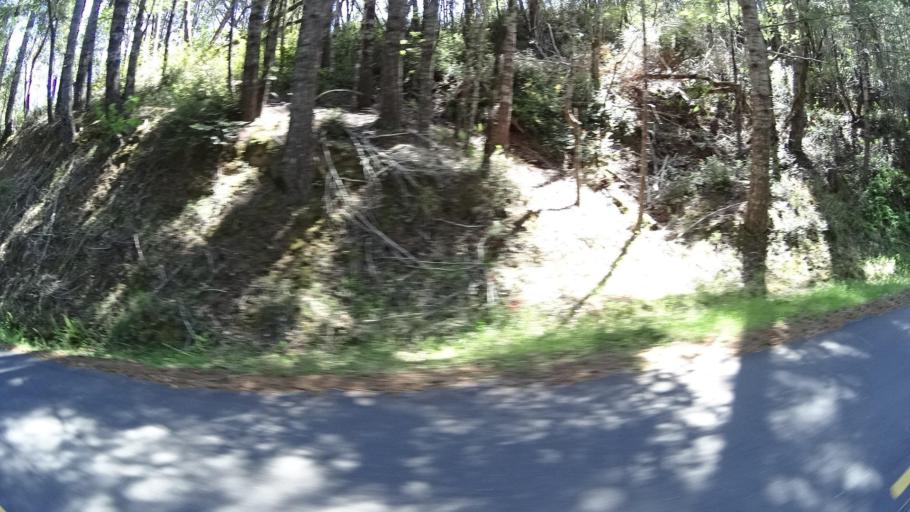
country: US
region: California
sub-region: Humboldt County
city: Rio Dell
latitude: 40.3262
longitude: -124.0490
